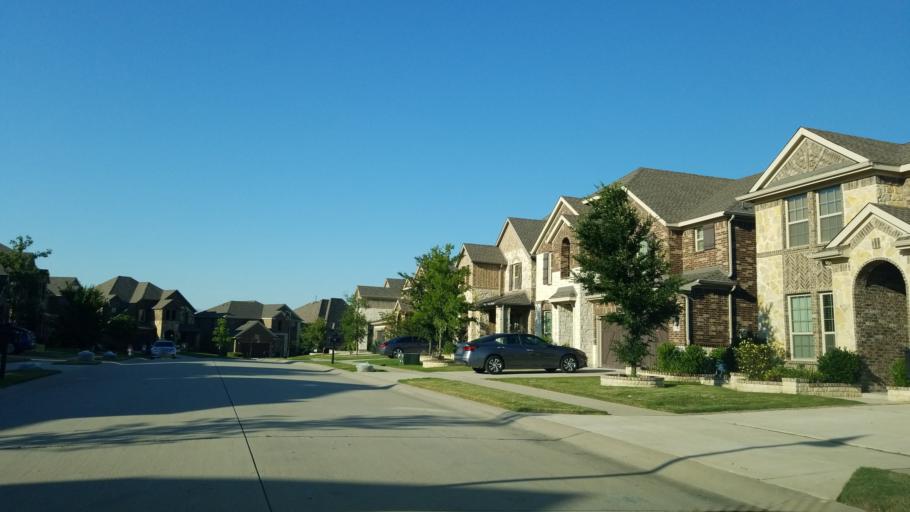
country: US
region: Texas
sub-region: Dallas County
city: Coppell
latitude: 32.9081
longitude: -96.9906
